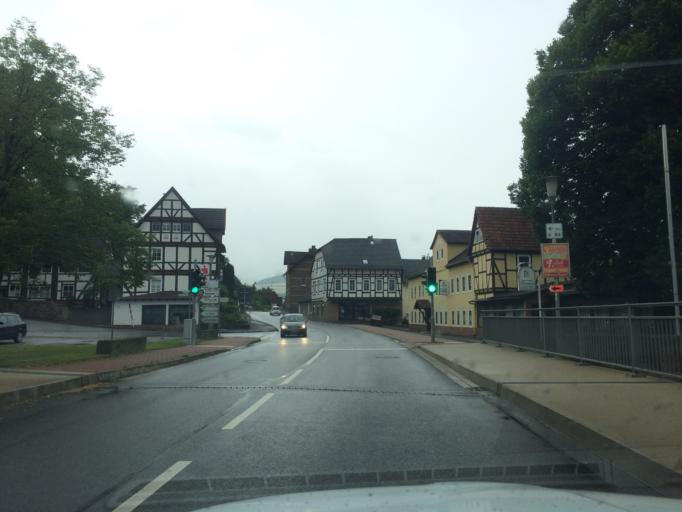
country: DE
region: Hesse
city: Trendelburg
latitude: 51.5751
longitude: 9.4284
